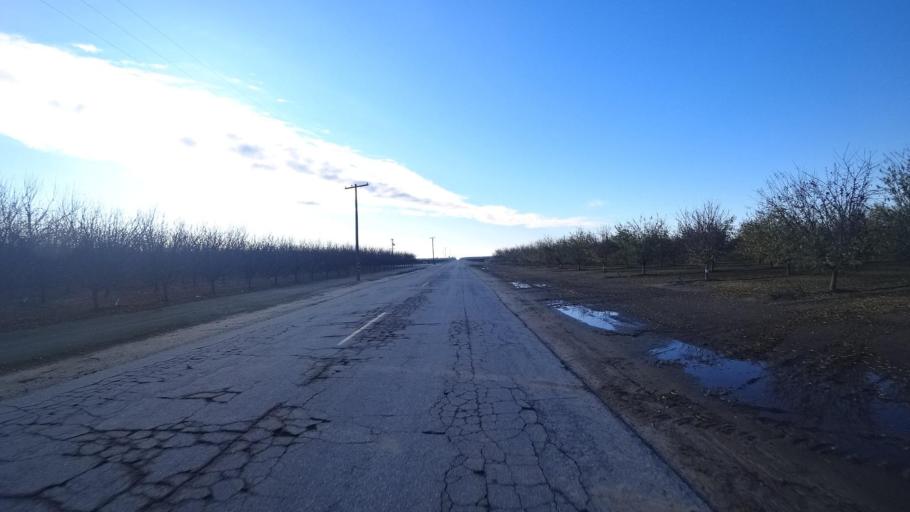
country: US
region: California
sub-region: Kern County
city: Delano
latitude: 35.7409
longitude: -119.3301
